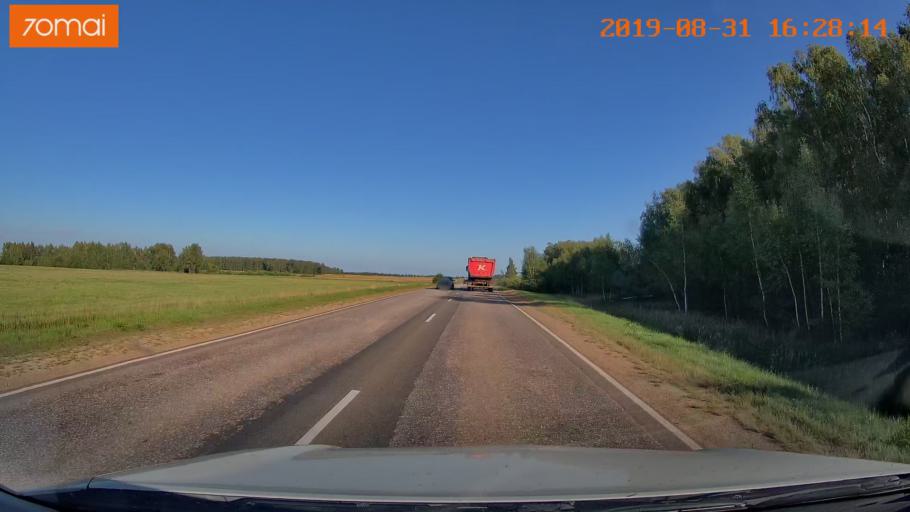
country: RU
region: Kaluga
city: Babynino
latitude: 54.5107
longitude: 35.7750
